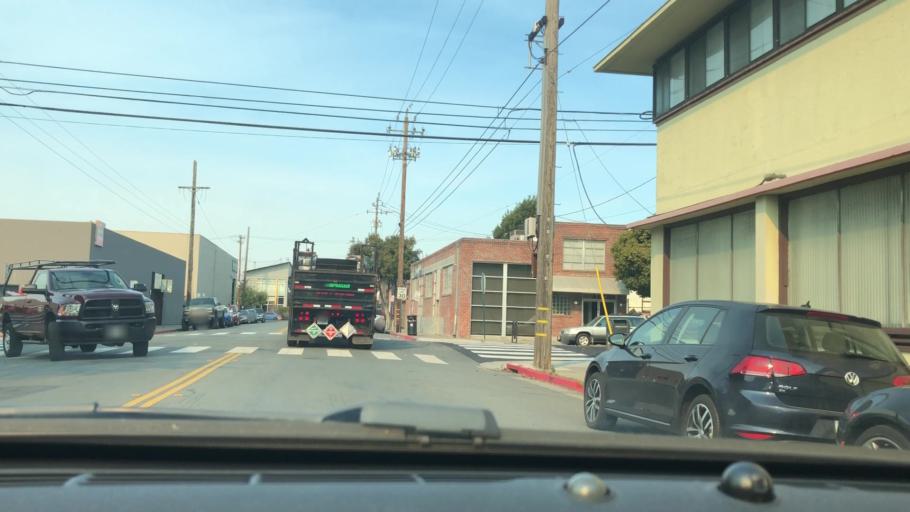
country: US
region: California
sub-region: Alameda County
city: Emeryville
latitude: 37.8486
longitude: -122.2921
